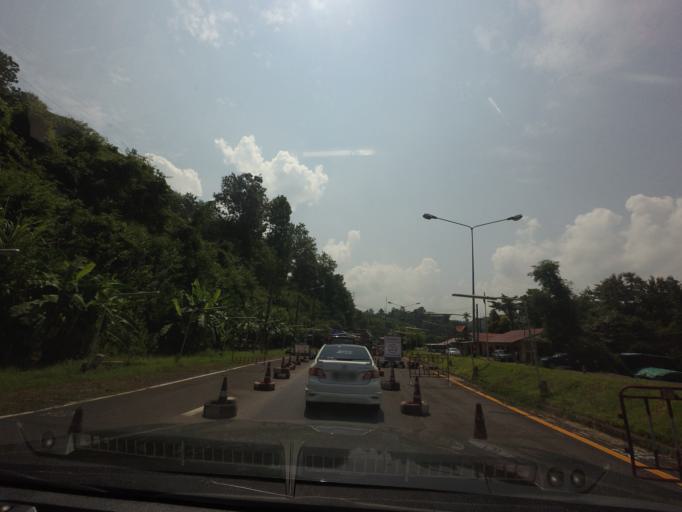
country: TH
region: Phrae
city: Den Chai
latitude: 17.8823
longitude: 100.0462
